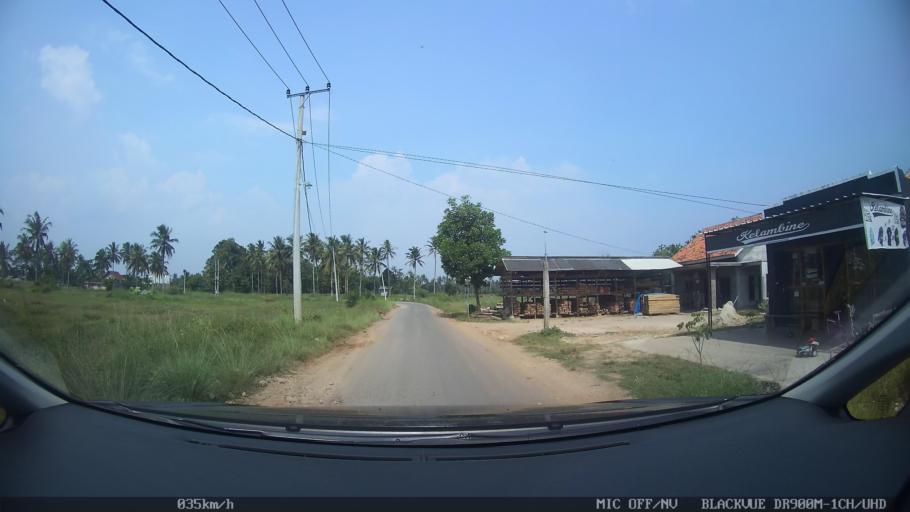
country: ID
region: Lampung
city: Natar
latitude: -5.3065
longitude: 105.2336
